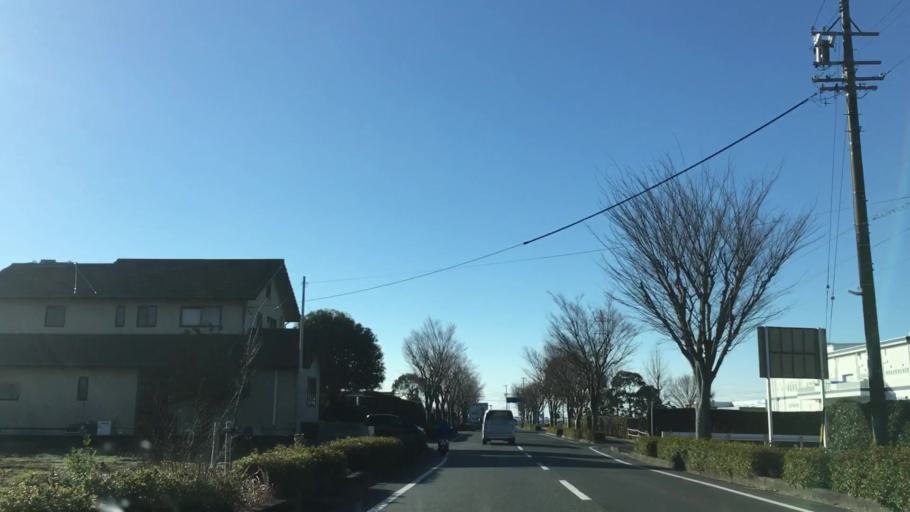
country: JP
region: Shizuoka
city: Hamakita
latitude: 34.8057
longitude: 137.7449
